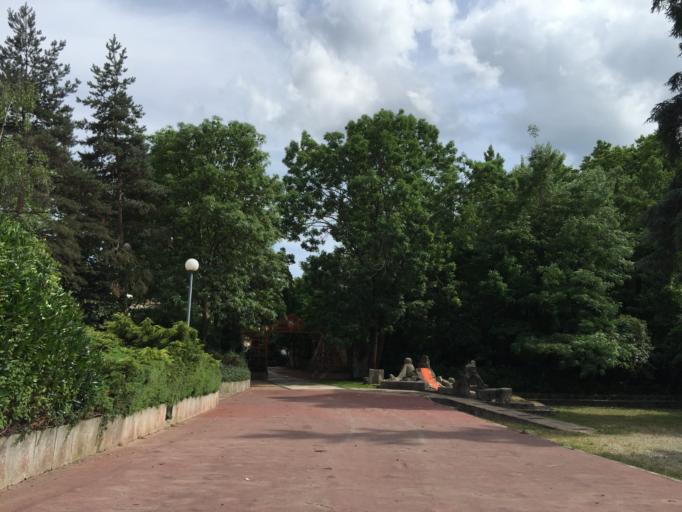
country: FR
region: Rhone-Alpes
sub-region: Departement de la Loire
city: Saint-Chamond
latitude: 45.4551
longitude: 4.5051
